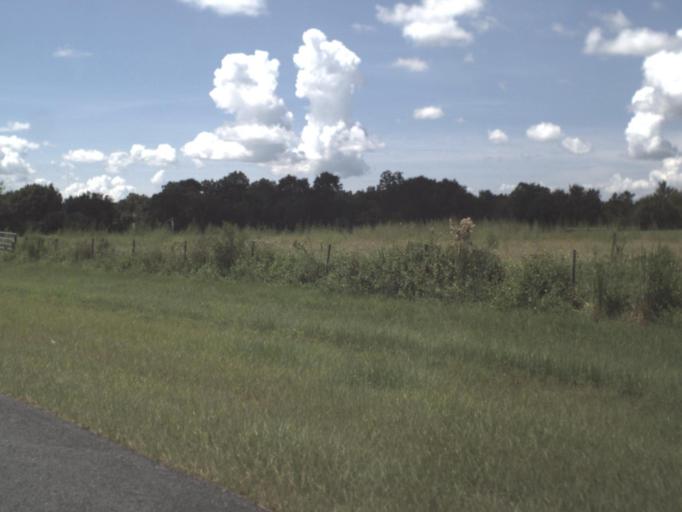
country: US
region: Florida
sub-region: Charlotte County
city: Harbour Heights
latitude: 27.0672
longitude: -81.9584
